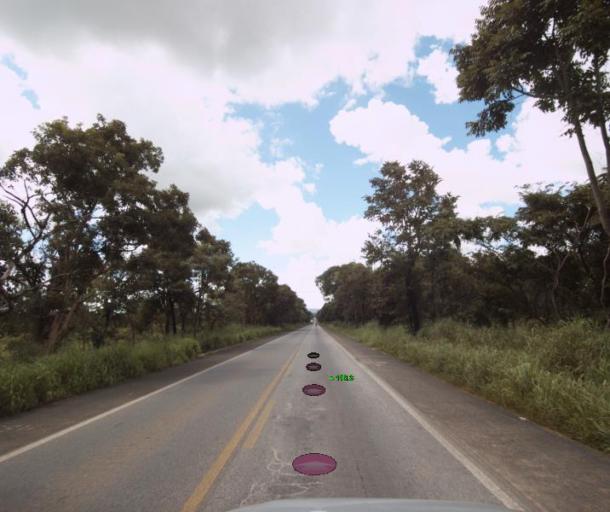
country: BR
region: Goias
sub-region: Porangatu
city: Porangatu
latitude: -13.7934
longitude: -49.0353
